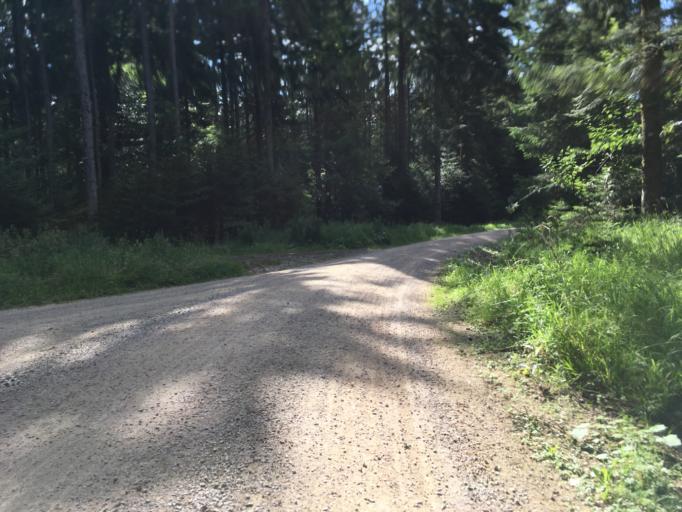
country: DE
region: Baden-Wuerttemberg
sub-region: Karlsruhe Region
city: Lossburg
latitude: 48.4307
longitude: 8.4320
